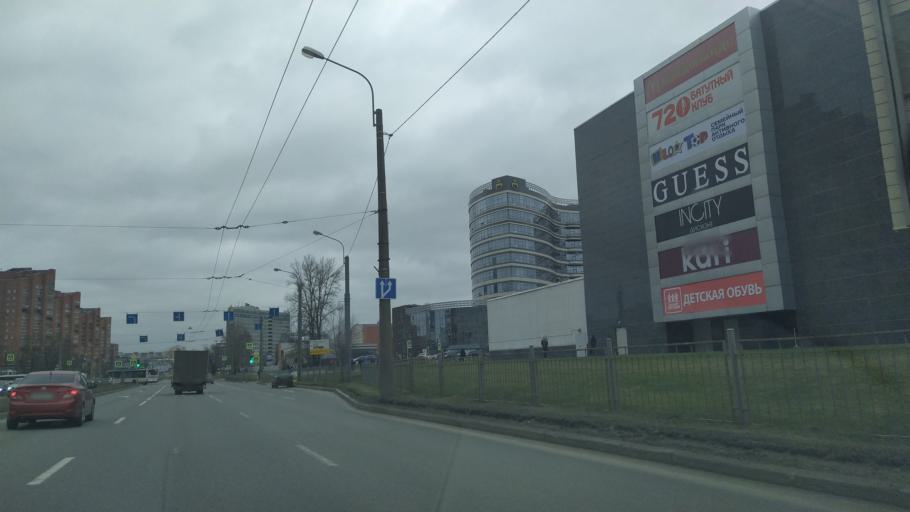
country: RU
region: St.-Petersburg
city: Kolomyagi
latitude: 60.0081
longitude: 30.2963
